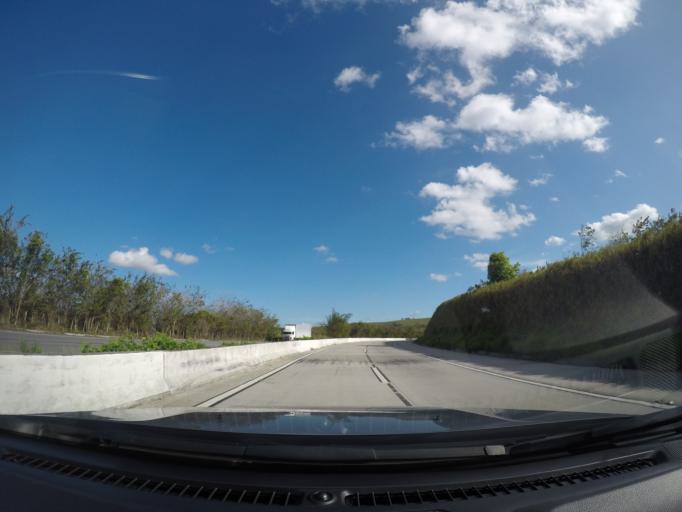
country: BR
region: Alagoas
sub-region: Flexeiras
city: Flexeiras
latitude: -9.2135
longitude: -35.7760
